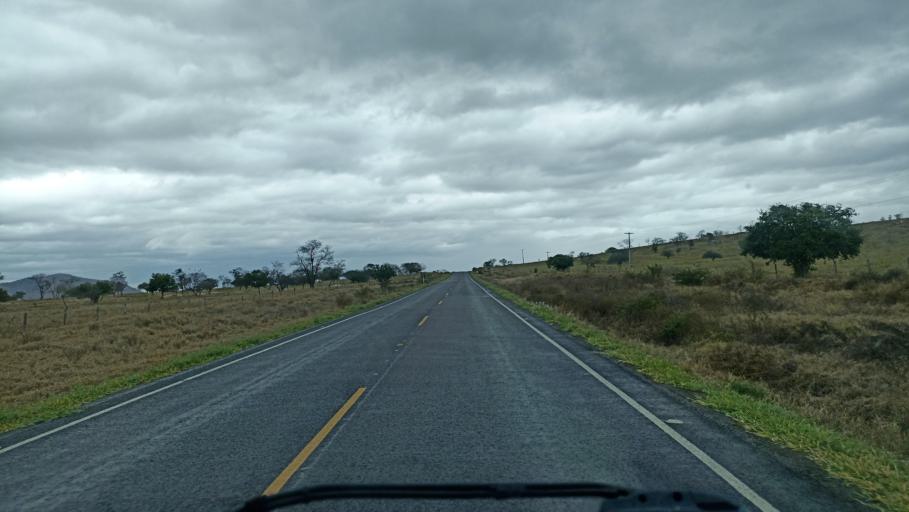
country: BR
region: Bahia
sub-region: Iacu
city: Iacu
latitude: -12.9653
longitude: -40.4883
